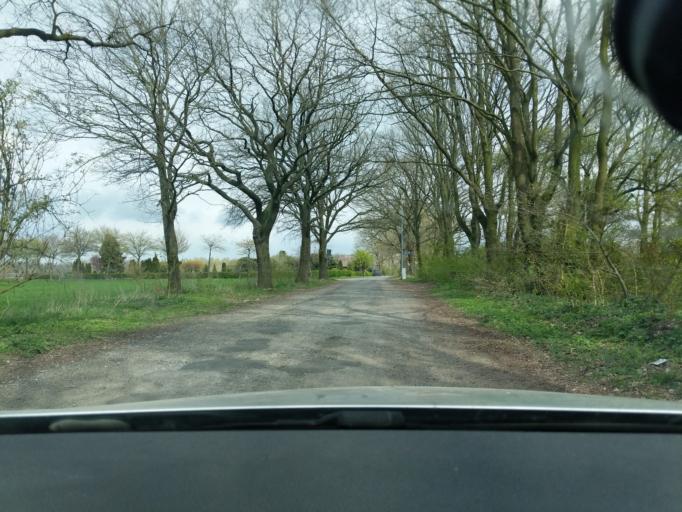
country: DE
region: Lower Saxony
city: Stade
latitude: 53.5714
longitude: 9.4651
